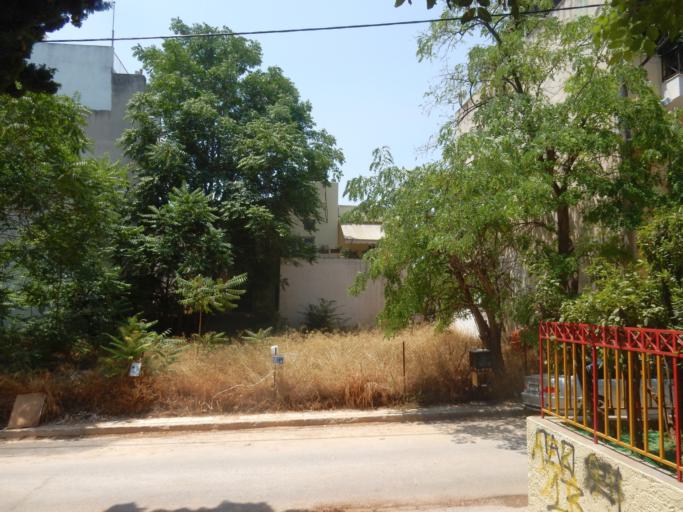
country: GR
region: Attica
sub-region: Nomarchia Athinas
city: Nea Filadelfeia
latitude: 38.0304
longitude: 23.7396
